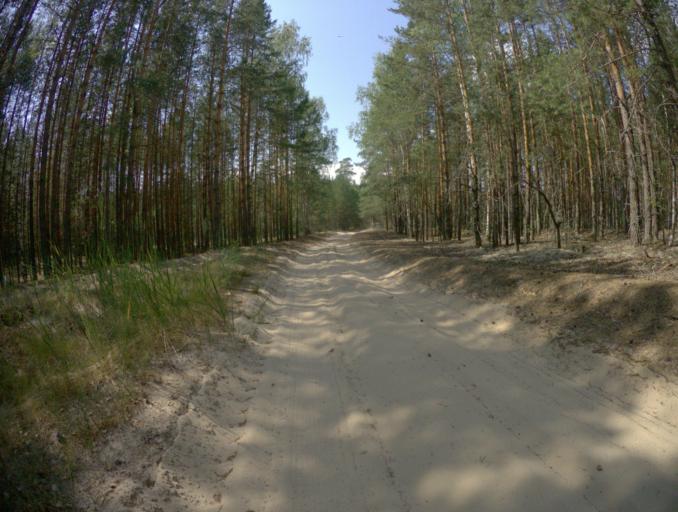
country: RU
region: Ivanovo
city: Talitsy
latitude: 56.4049
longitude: 42.3617
